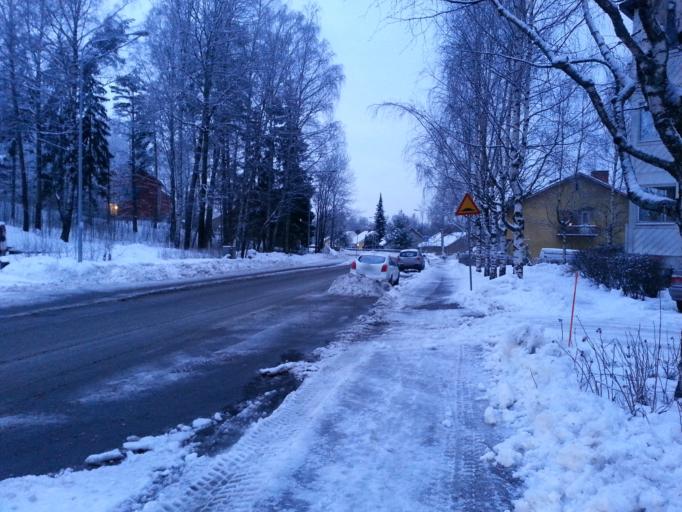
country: FI
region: Uusimaa
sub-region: Helsinki
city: Teekkarikylae
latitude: 60.2339
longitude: 24.8439
